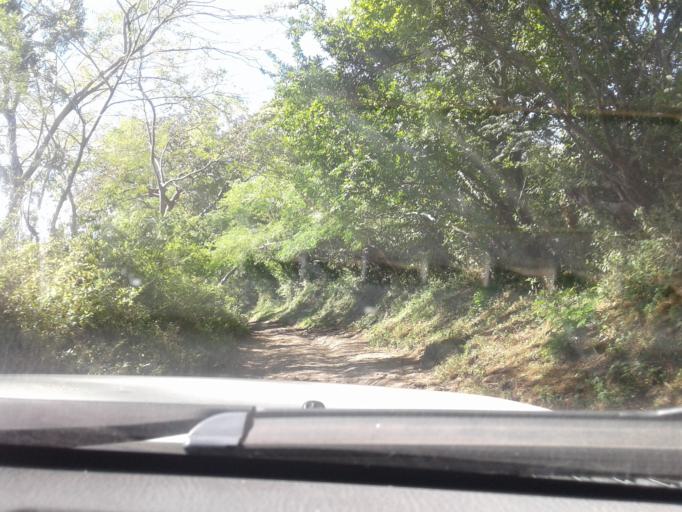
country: NI
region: Carazo
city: Santa Teresa
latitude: 11.7884
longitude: -86.1850
